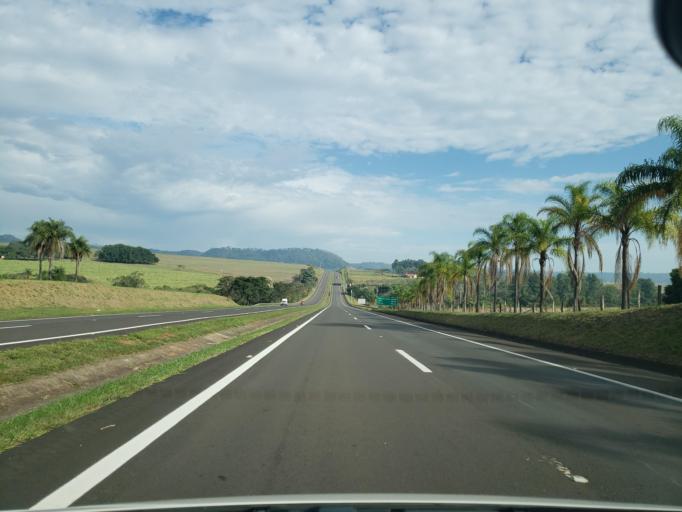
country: BR
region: Sao Paulo
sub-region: Dois Corregos
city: Dois Corregos
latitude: -22.2444
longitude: -48.3092
